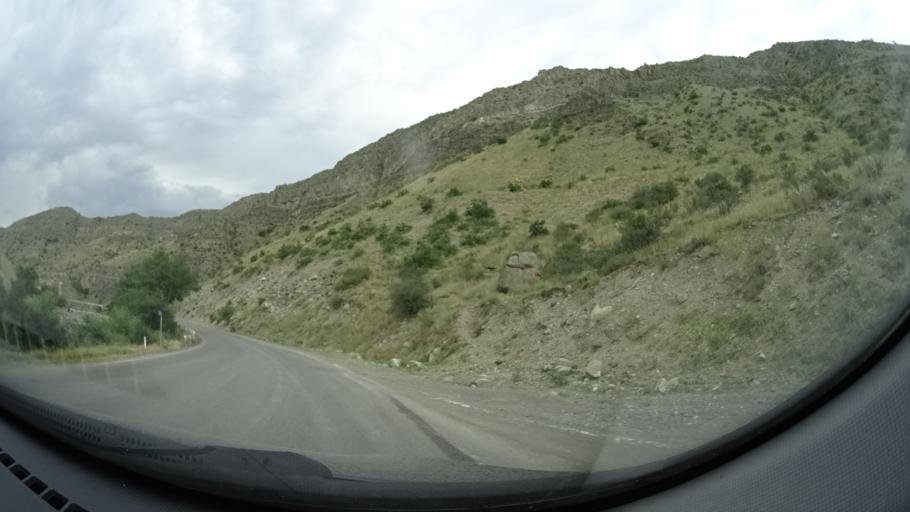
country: GE
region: Samtskhe-Javakheti
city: Aspindza
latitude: 41.6055
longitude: 43.1466
